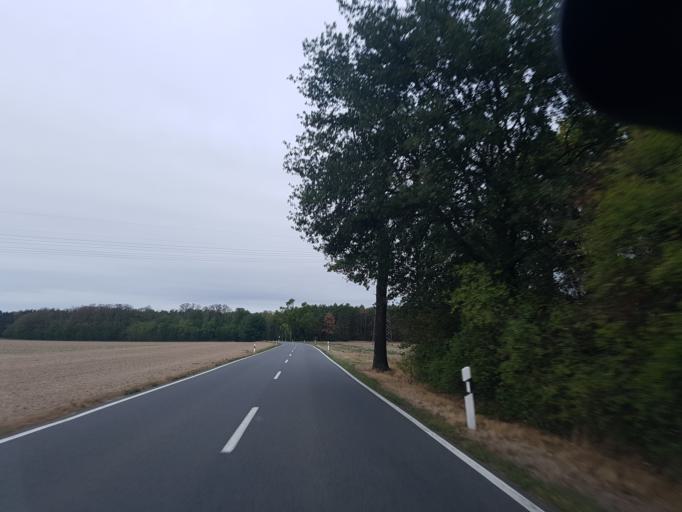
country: DE
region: Saxony-Anhalt
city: Prettin
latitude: 51.6530
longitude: 12.9643
